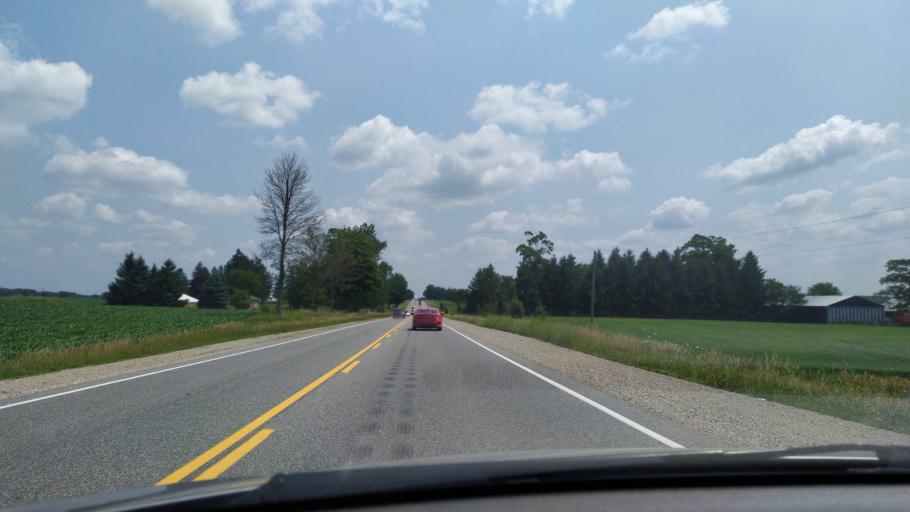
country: CA
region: Ontario
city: Stratford
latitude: 43.3692
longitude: -80.7961
